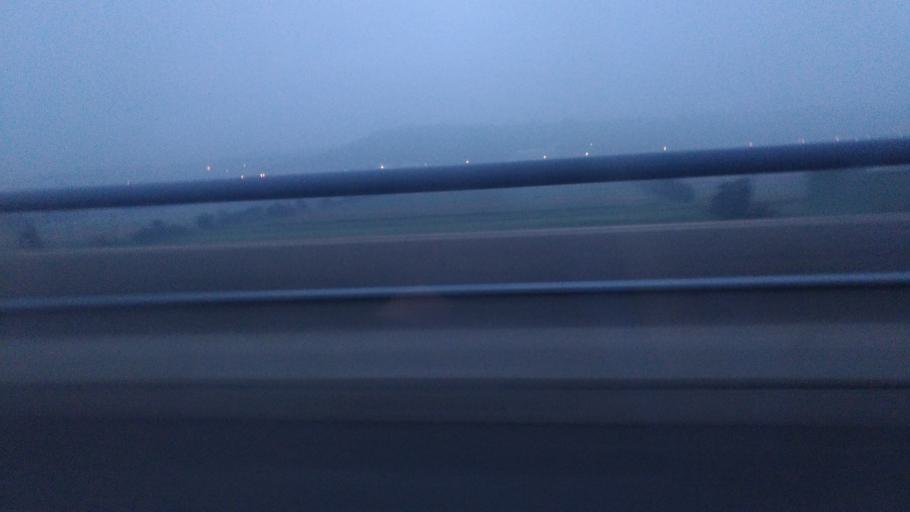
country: TW
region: Taiwan
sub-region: Miaoli
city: Miaoli
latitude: 24.4684
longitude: 120.6583
